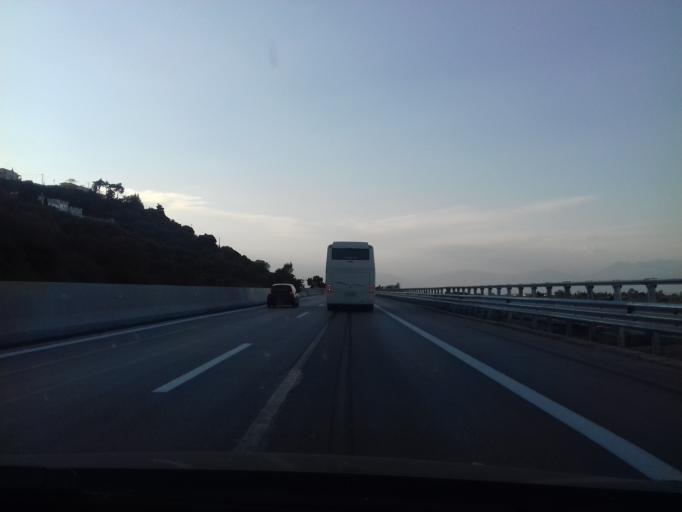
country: GR
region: West Greece
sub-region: Nomos Achaias
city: Siliveniotika
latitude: 38.1604
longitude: 22.3379
